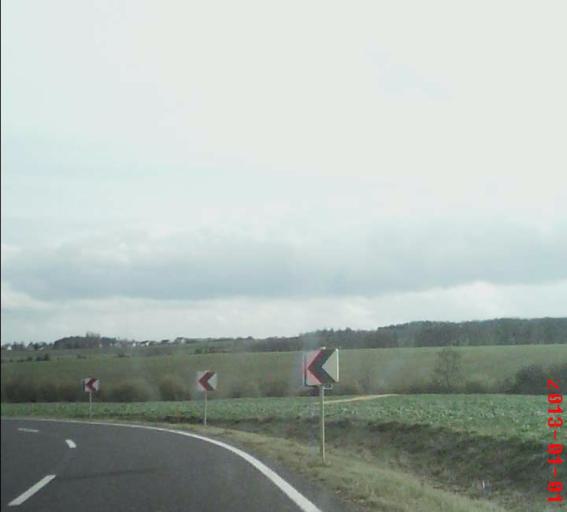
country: DE
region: Thuringia
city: Anrode
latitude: 51.2447
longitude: 10.3569
